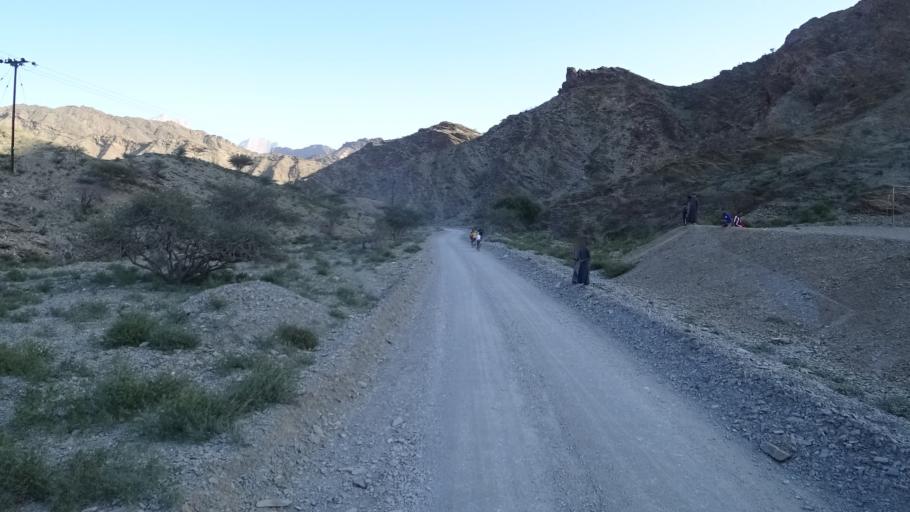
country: OM
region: Al Batinah
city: Rustaq
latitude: 23.2687
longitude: 57.3913
